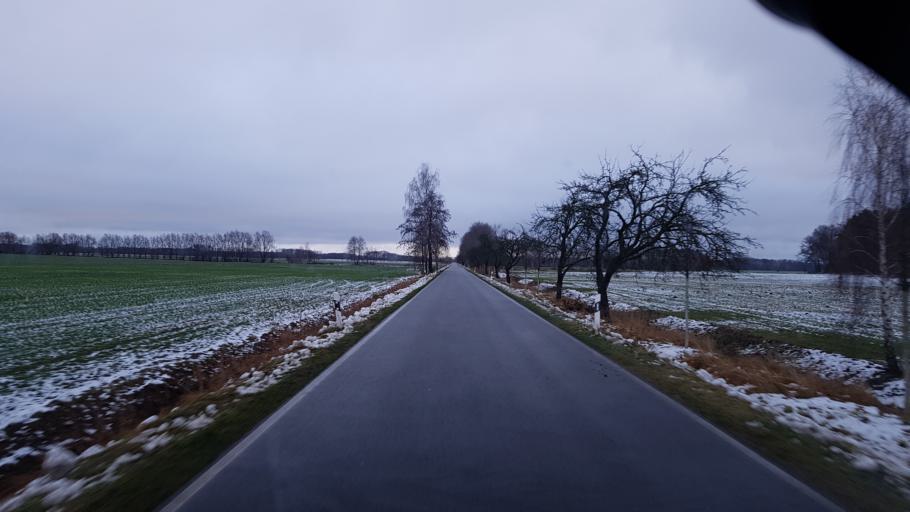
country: DE
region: Brandenburg
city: Luckau
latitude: 51.8131
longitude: 13.7071
